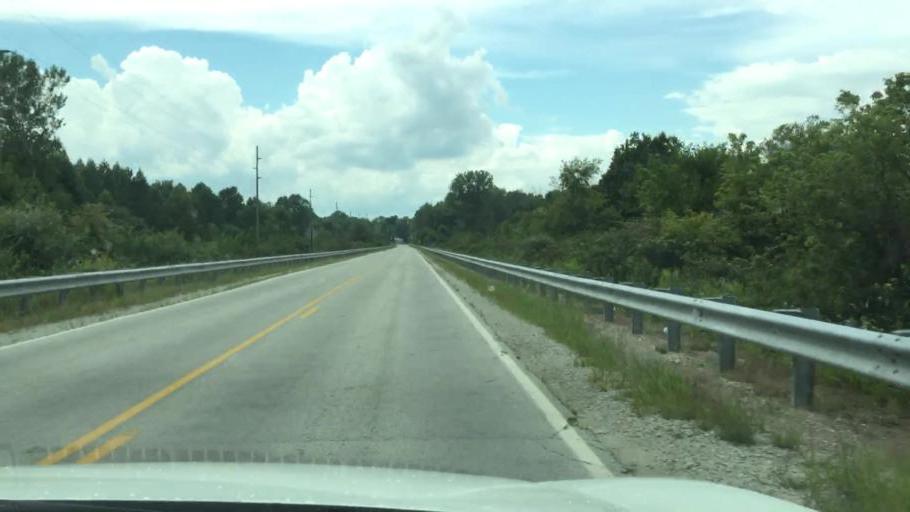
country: US
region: Ohio
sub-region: Clark County
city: Northridge
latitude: 39.9915
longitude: -83.7057
